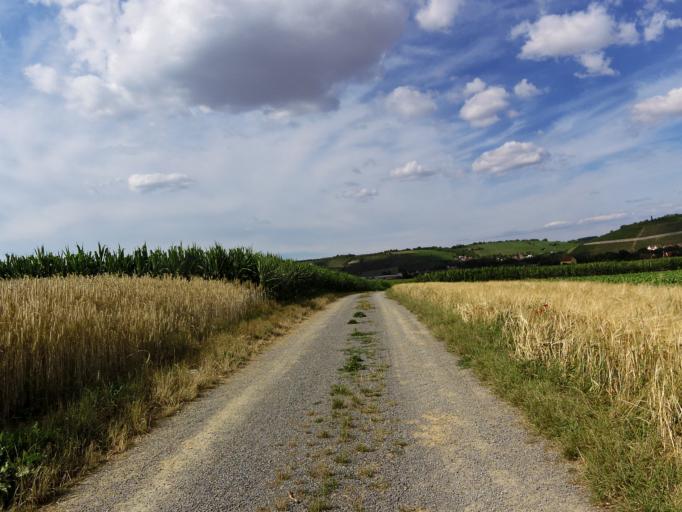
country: DE
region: Bavaria
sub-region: Regierungsbezirk Unterfranken
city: Randersacker
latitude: 49.7465
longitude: 9.9749
